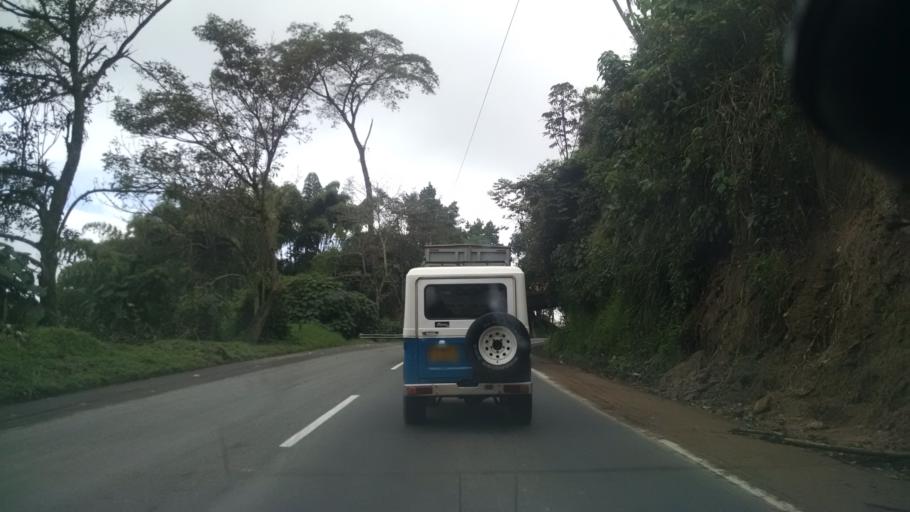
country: CO
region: Caldas
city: Chinchina
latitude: 5.0028
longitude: -75.5959
